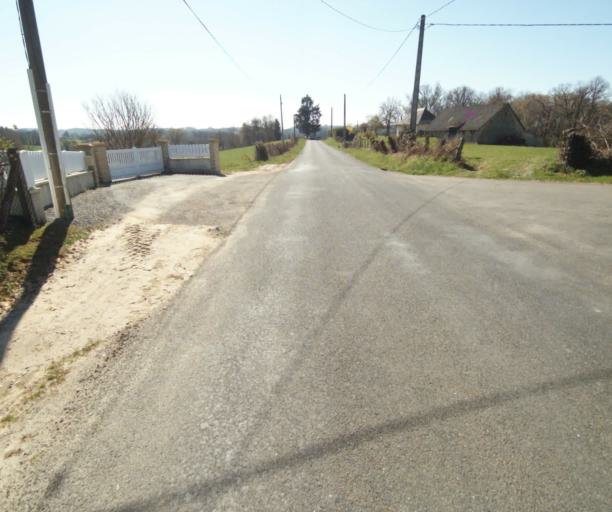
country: FR
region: Limousin
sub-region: Departement de la Correze
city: Saint-Mexant
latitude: 45.3159
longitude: 1.6465
